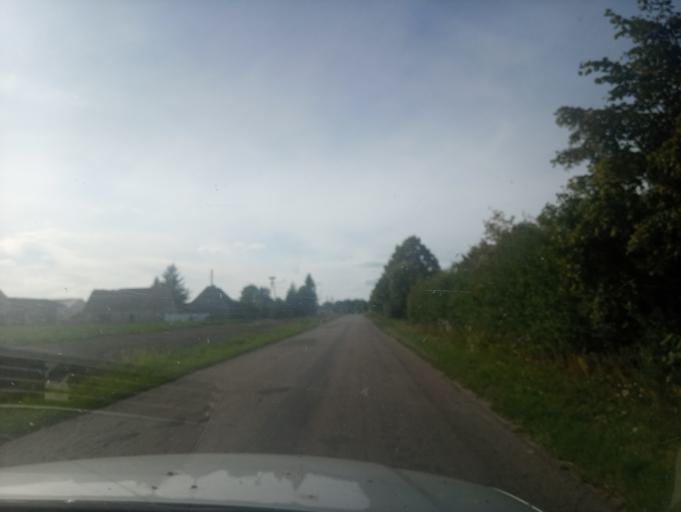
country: PL
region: Greater Poland Voivodeship
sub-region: Powiat pilski
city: Lobzenica
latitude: 53.2262
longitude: 17.3295
